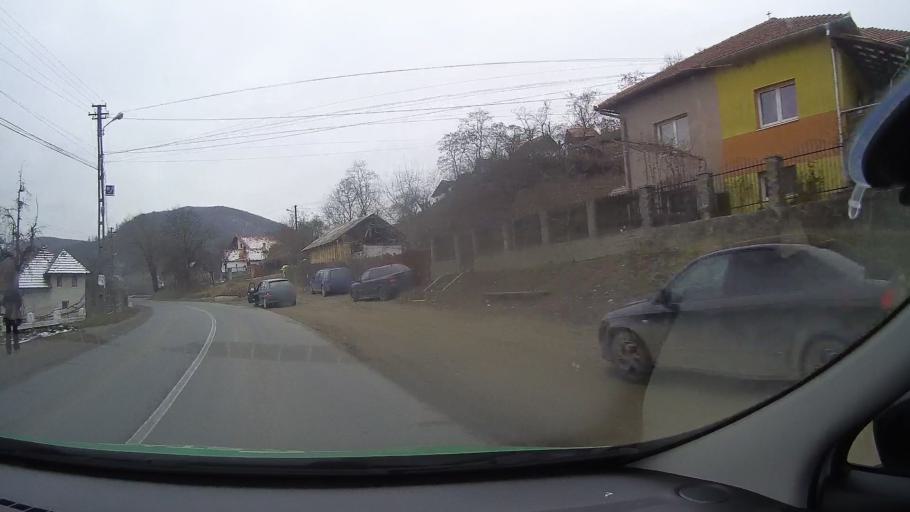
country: RO
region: Alba
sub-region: Comuna Metes
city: Metes
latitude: 46.0987
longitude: 23.4585
